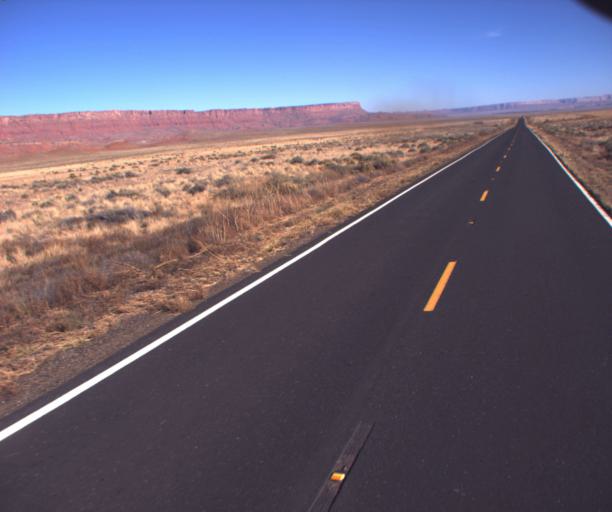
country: US
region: Arizona
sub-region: Coconino County
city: Fredonia
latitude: 36.7282
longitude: -112.0362
